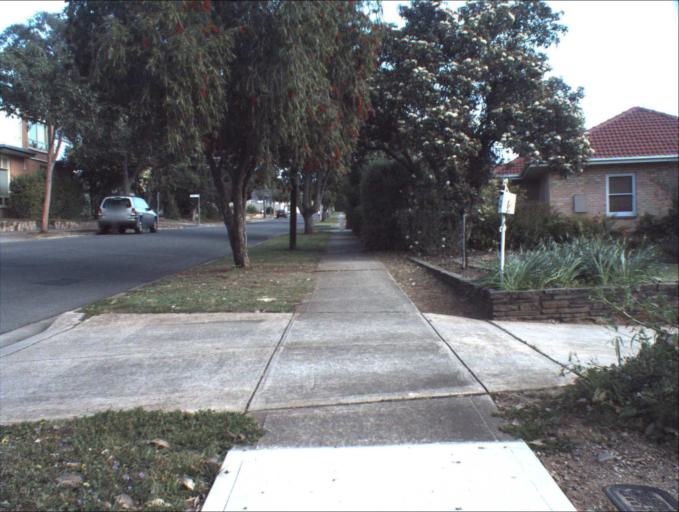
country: AU
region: South Australia
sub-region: Port Adelaide Enfield
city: Klemzig
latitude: -34.8821
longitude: 138.6296
